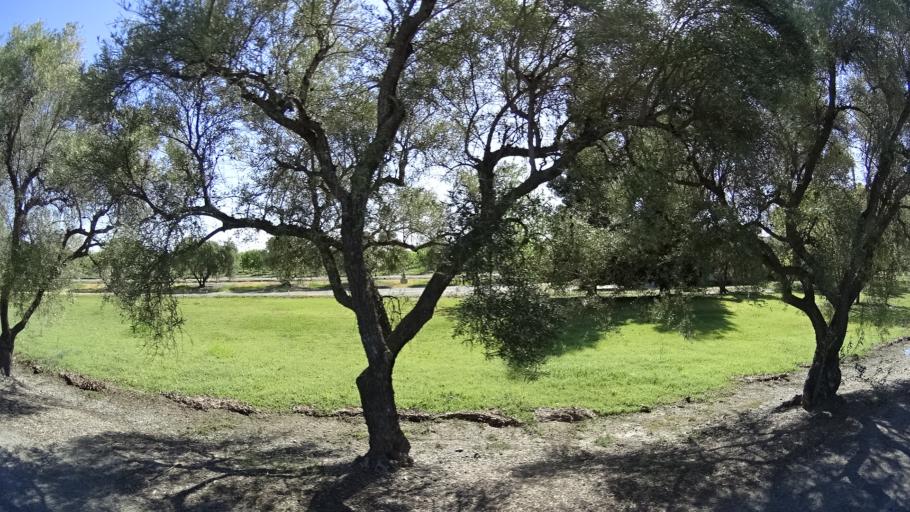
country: US
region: California
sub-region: Glenn County
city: Orland
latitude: 39.7336
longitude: -122.1688
